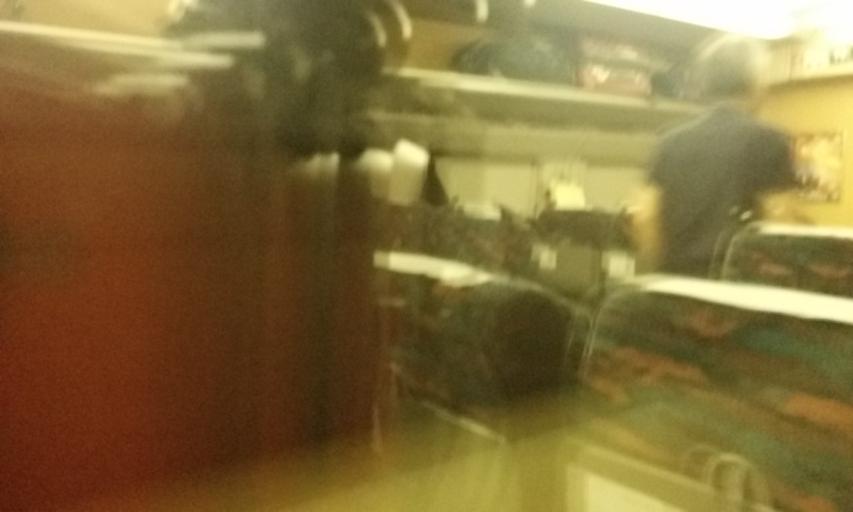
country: JP
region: Fukushima
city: Nihommatsu
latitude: 37.5378
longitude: 140.4438
